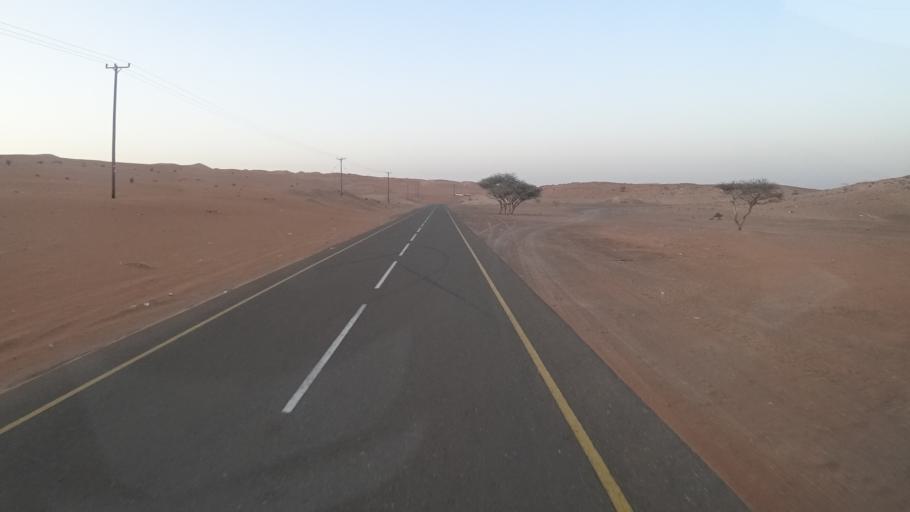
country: OM
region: Ash Sharqiyah
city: Badiyah
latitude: 22.4793
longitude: 58.7117
